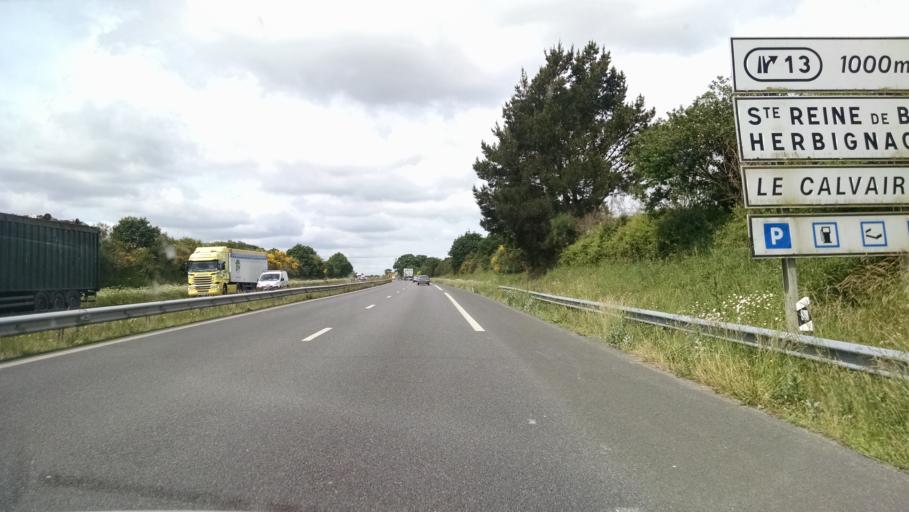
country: FR
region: Pays de la Loire
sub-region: Departement de la Loire-Atlantique
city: Pontchateau
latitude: 47.4481
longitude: -2.1055
